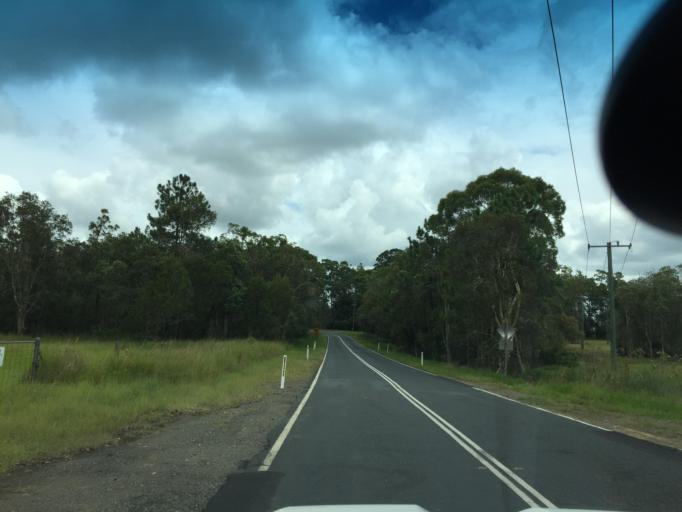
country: AU
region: Queensland
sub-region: Moreton Bay
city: Caboolture
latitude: -27.0438
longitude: 152.9170
